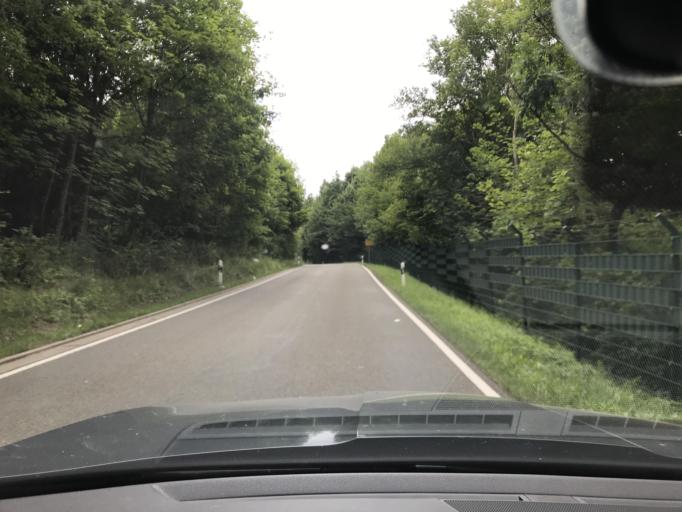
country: DE
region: Saxony-Anhalt
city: Harzgerode
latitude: 51.6340
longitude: 11.0973
